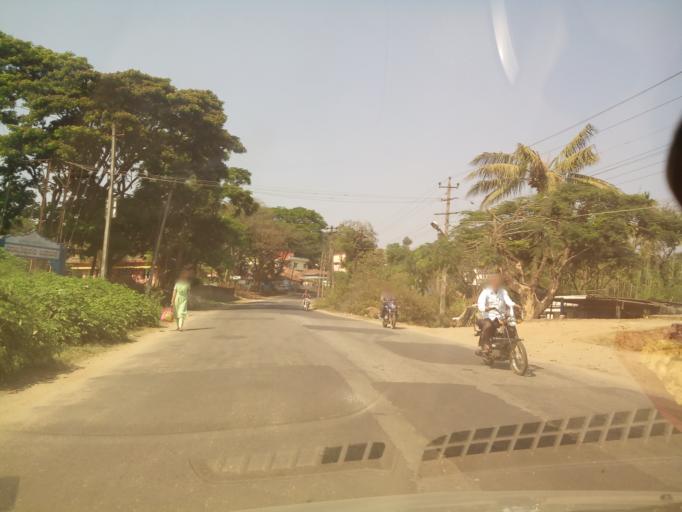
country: IN
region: Karnataka
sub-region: Hassan
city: Sakleshpur
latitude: 12.9465
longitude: 75.8006
